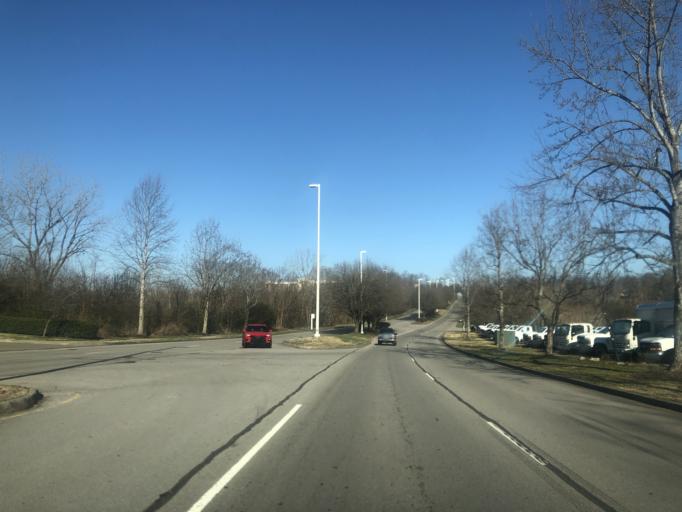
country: US
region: Tennessee
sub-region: Rutherford County
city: La Vergne
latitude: 36.0405
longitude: -86.6460
